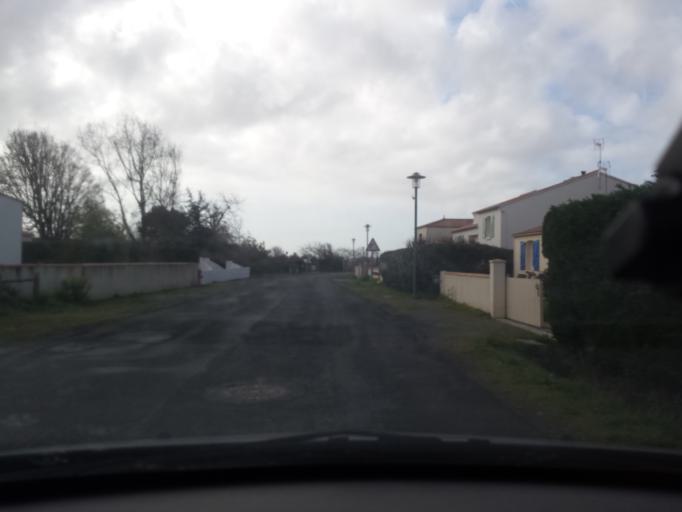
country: FR
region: Pays de la Loire
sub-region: Departement de la Vendee
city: Olonne-sur-Mer
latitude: 46.5614
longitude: -1.7839
